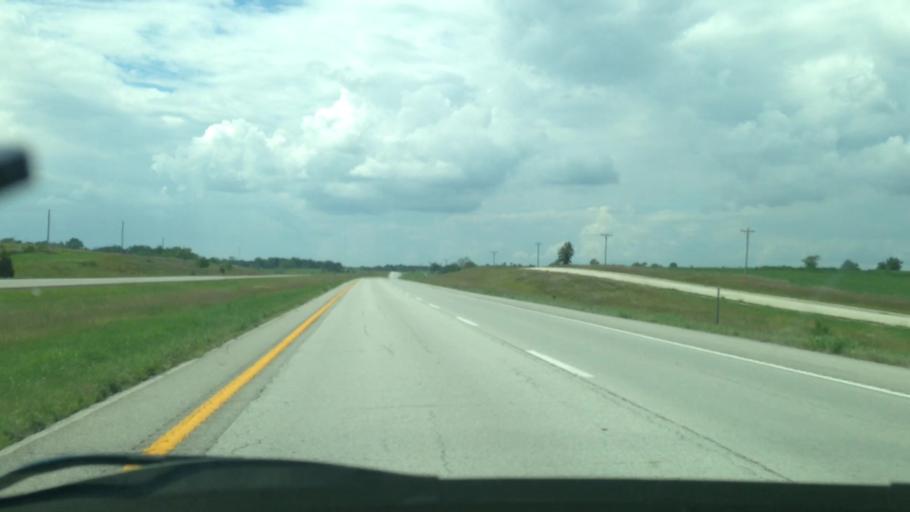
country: US
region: Missouri
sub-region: Pike County
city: Bowling Green
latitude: 39.2518
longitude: -91.0394
